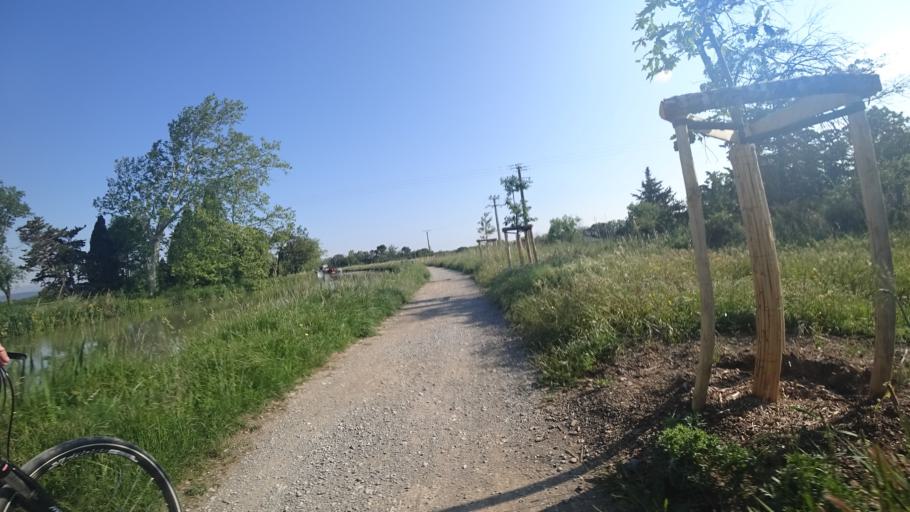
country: FR
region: Languedoc-Roussillon
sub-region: Departement de l'Aude
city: Saint-Marcel-sur-Aude
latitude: 43.2749
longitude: 2.9154
